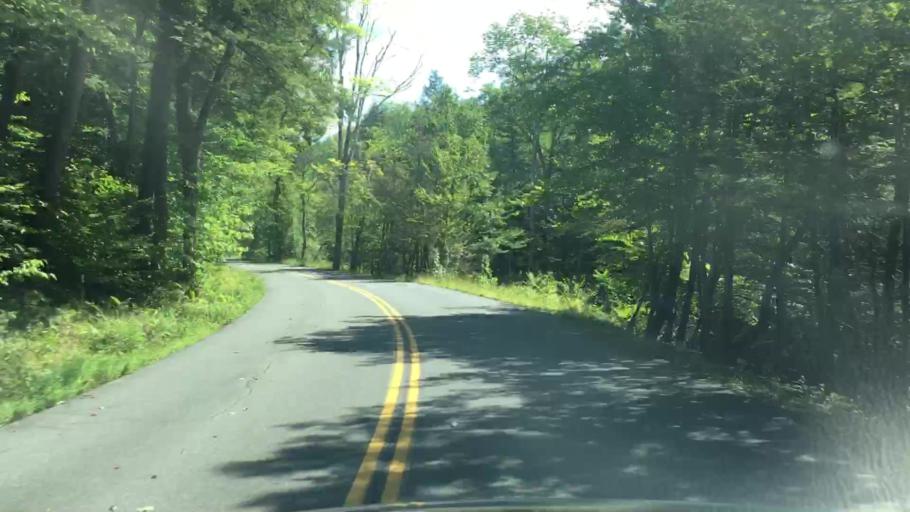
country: US
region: Vermont
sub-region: Windham County
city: West Brattleboro
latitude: 42.8032
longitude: -72.6950
